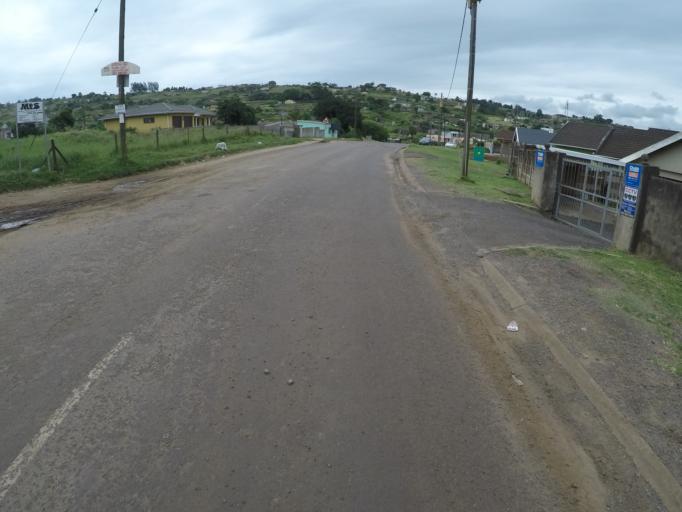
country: ZA
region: KwaZulu-Natal
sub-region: uThungulu District Municipality
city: Empangeni
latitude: -28.7737
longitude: 31.8488
